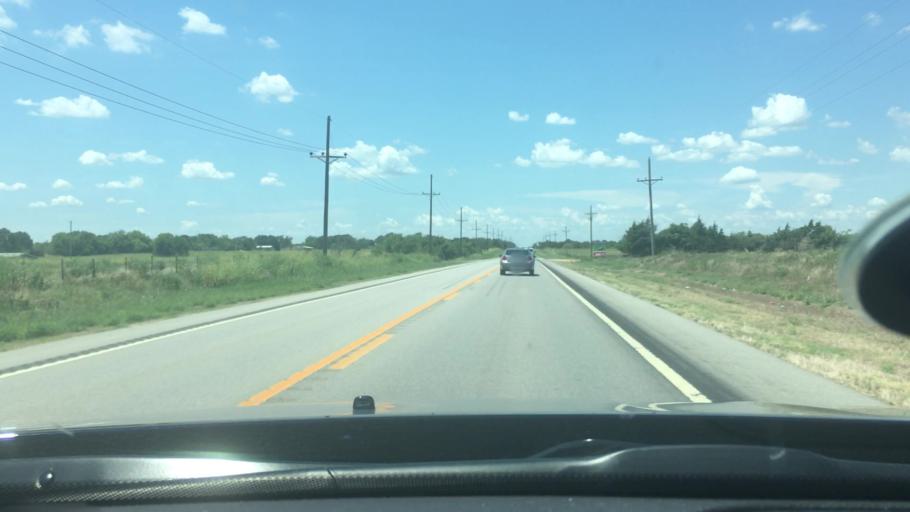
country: US
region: Oklahoma
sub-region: Bryan County
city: Durant
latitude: 33.9976
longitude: -96.2666
